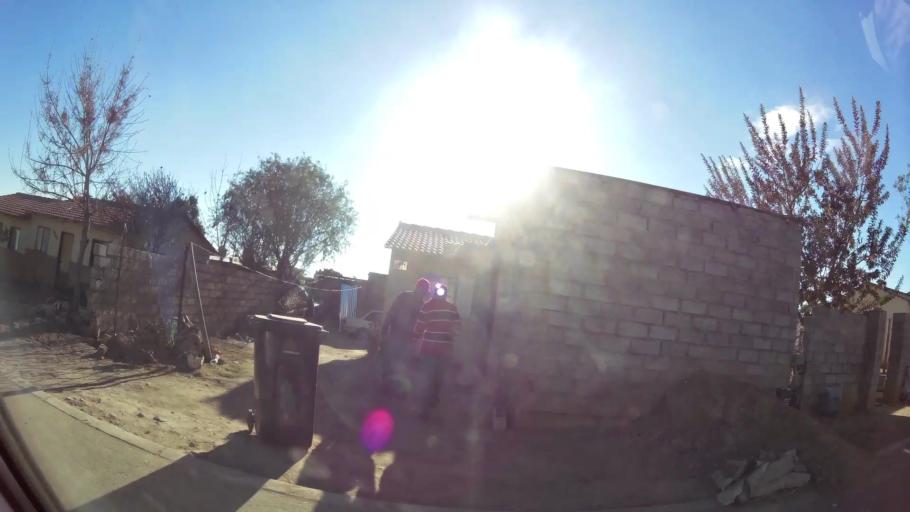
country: ZA
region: Gauteng
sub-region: City of Johannesburg Metropolitan Municipality
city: Diepsloot
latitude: -25.8981
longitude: 28.0961
